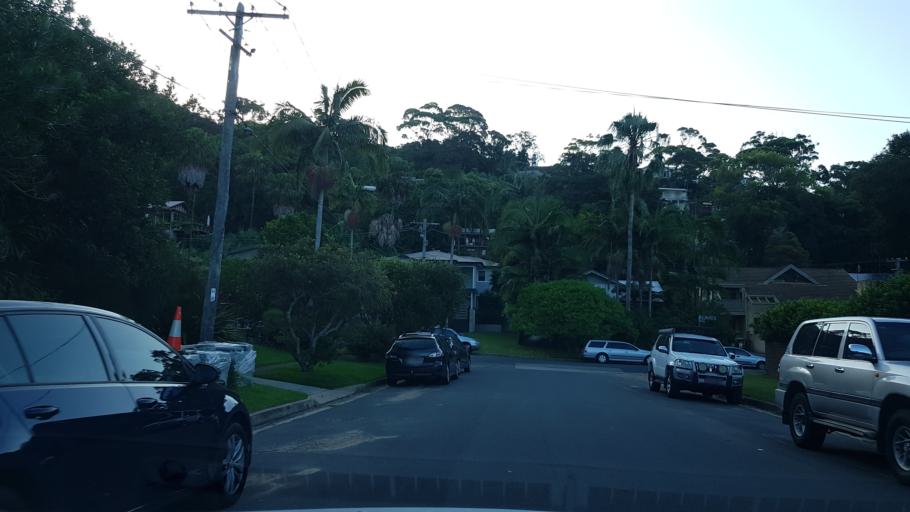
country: AU
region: New South Wales
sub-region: Warringah
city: Narrabeen
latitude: -33.7227
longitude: 151.2923
